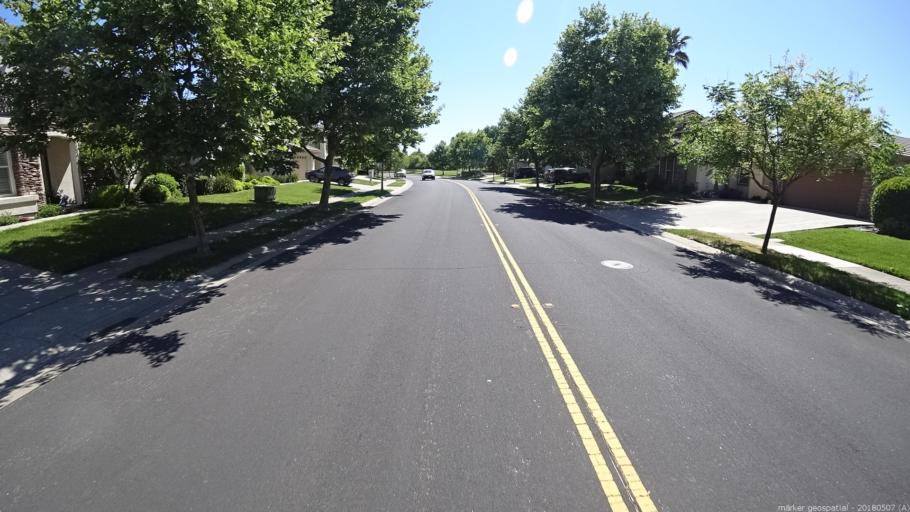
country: US
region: California
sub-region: Sacramento County
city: Rio Linda
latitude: 38.6597
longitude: -121.4980
